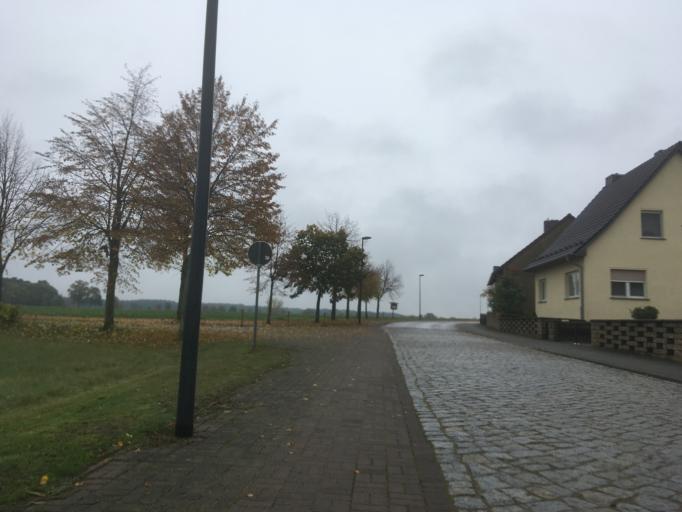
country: DE
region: Brandenburg
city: Neu Zauche
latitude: 52.0301
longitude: 14.0806
